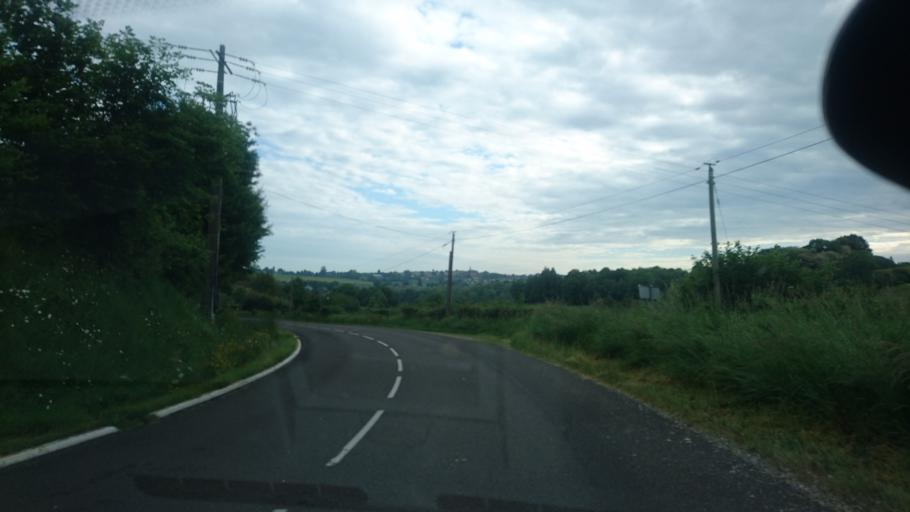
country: FR
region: Limousin
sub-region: Departement de la Haute-Vienne
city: Saint-Germain-les-Belles
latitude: 45.5969
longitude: 1.4831
